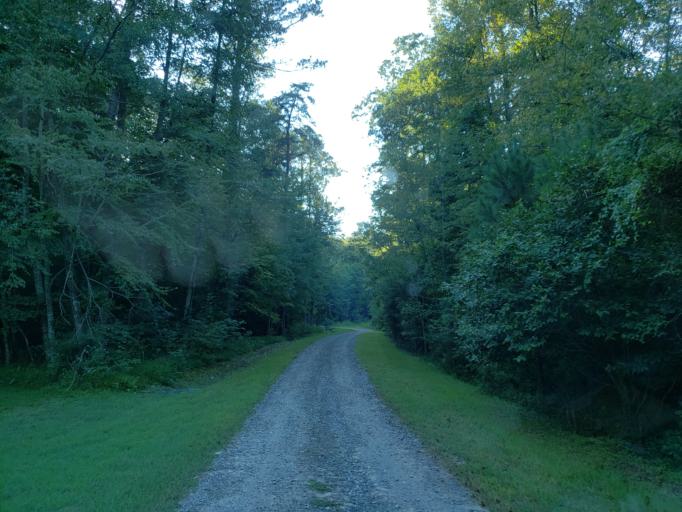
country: US
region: Georgia
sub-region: Fannin County
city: Blue Ridge
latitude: 34.6899
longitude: -84.2732
